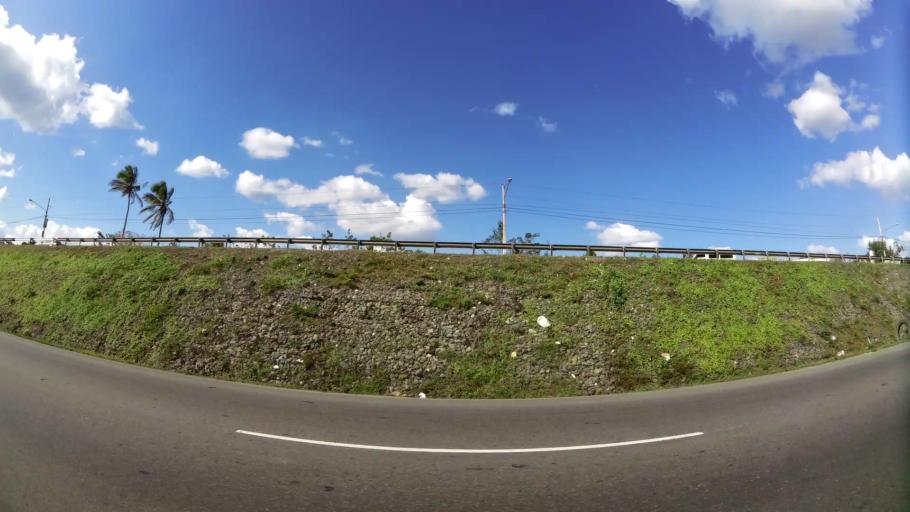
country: DO
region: Santo Domingo
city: Santo Domingo Oeste
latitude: 18.5370
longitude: -70.0186
